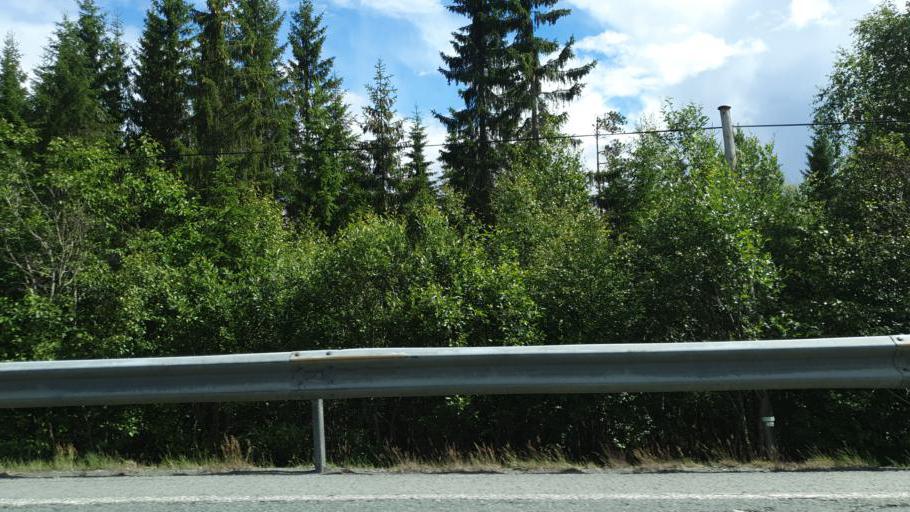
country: NO
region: Sor-Trondelag
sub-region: Rennebu
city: Berkak
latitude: 62.7062
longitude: 9.9532
